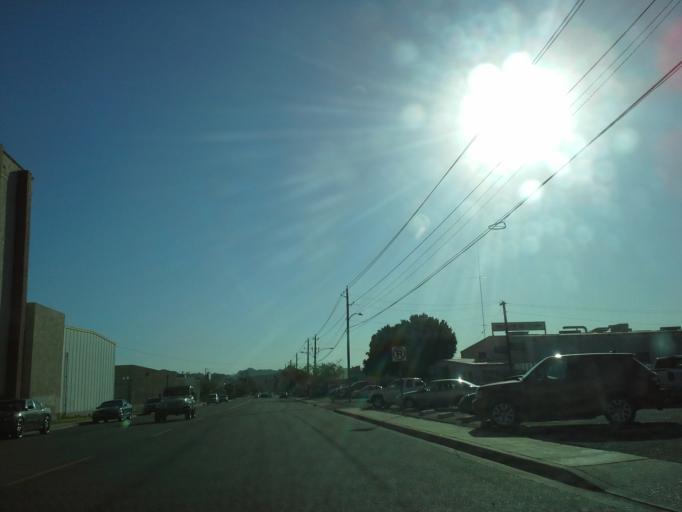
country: US
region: Arizona
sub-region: Maricopa County
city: Glendale
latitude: 33.5748
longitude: -112.1024
